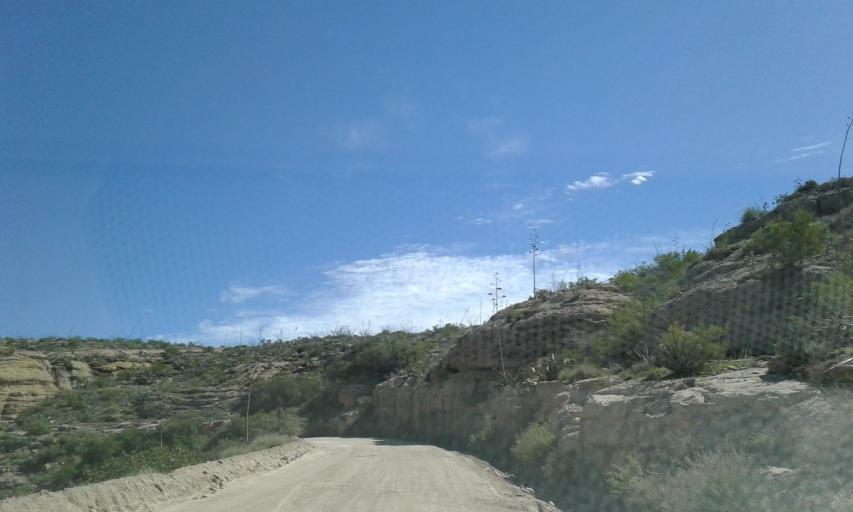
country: US
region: Arizona
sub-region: Pinal County
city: Gold Camp
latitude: 33.5288
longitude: -111.3167
